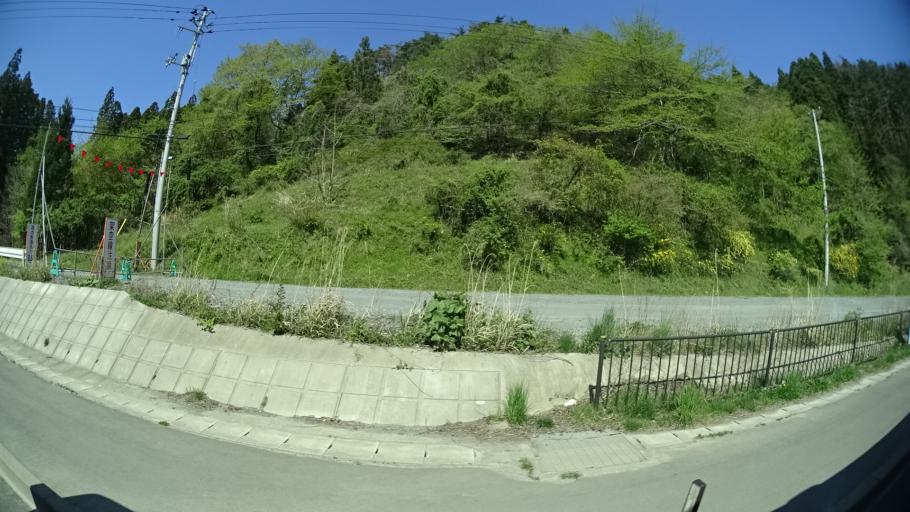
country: JP
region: Iwate
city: Ofunato
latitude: 38.9539
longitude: 141.6296
